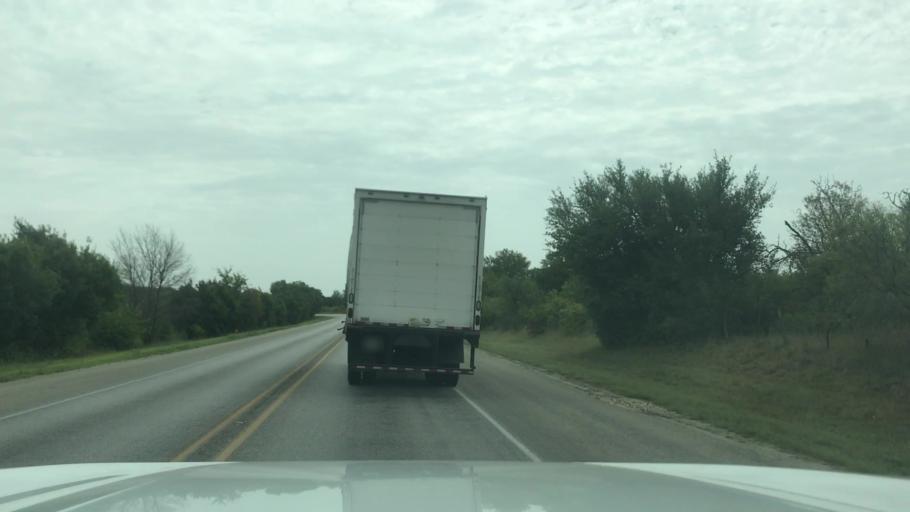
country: US
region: Texas
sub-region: Erath County
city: Dublin
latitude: 32.0892
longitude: -98.4368
